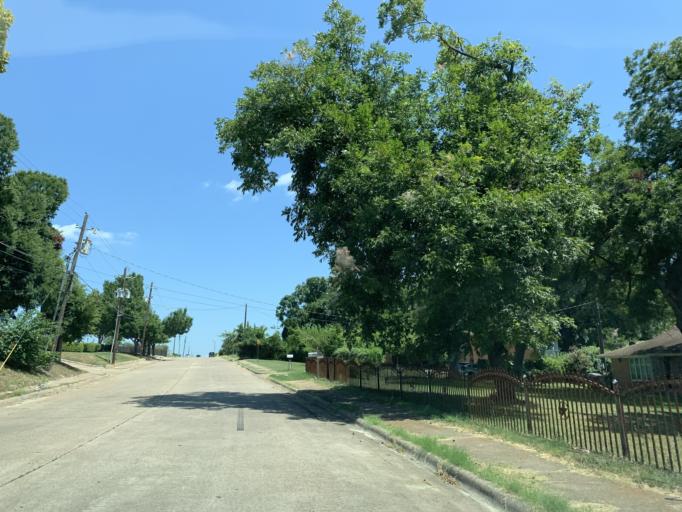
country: US
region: Texas
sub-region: Dallas County
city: Hutchins
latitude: 32.6911
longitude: -96.7708
